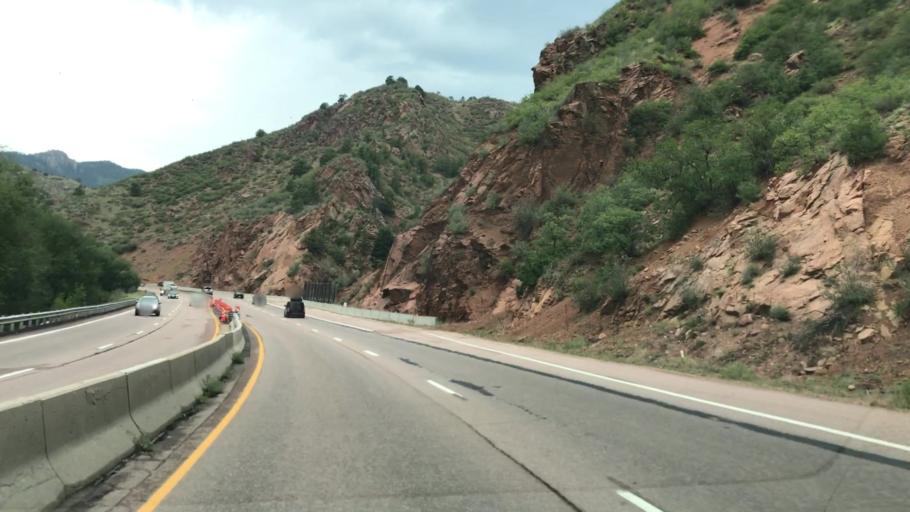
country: US
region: Colorado
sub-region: El Paso County
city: Manitou Springs
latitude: 38.8762
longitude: -104.9306
